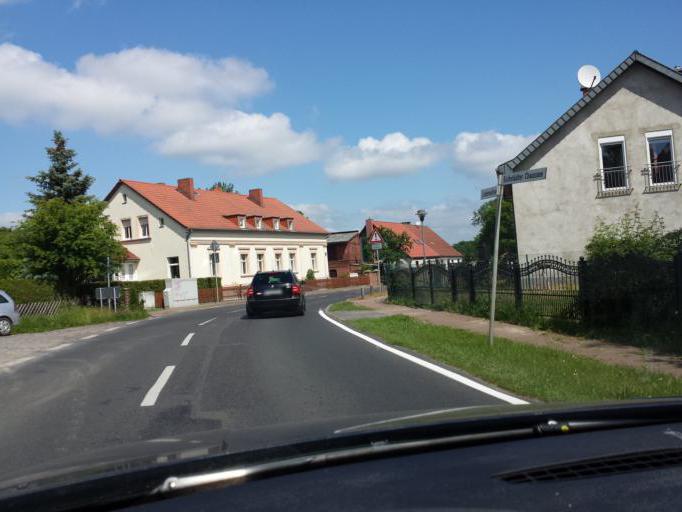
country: DE
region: Brandenburg
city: Velten
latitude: 52.7142
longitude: 13.1012
